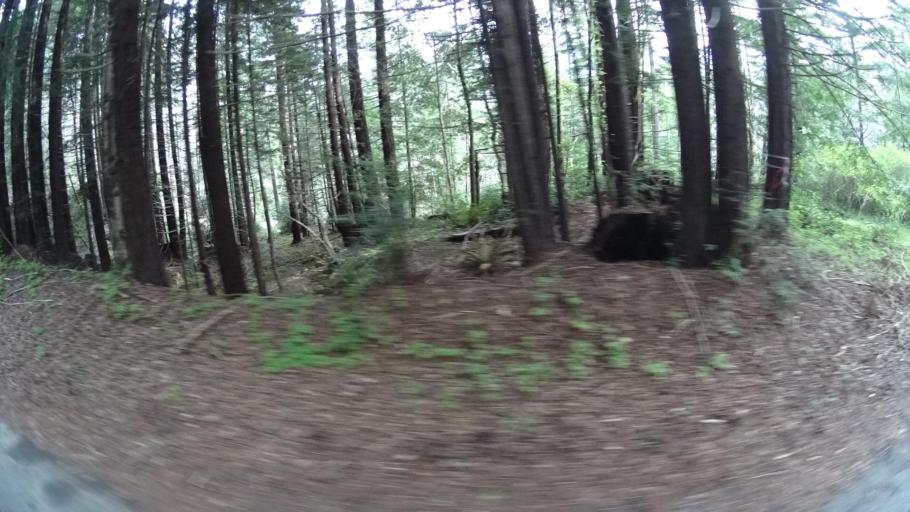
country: US
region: California
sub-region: Humboldt County
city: Redway
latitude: 40.3362
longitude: -123.8578
